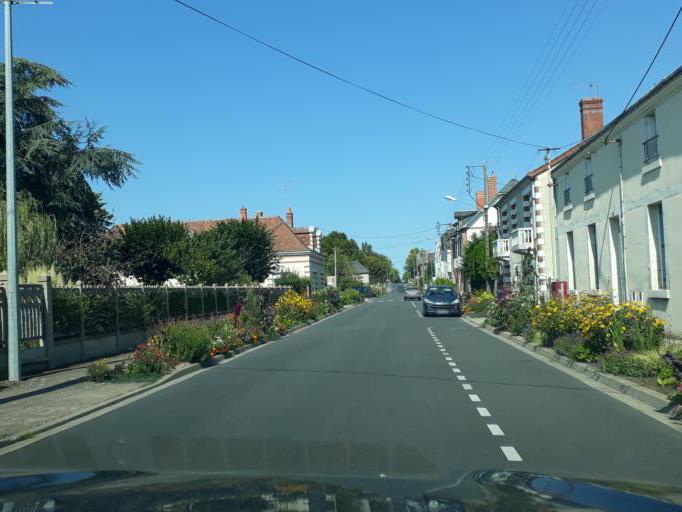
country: FR
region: Centre
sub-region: Departement de l'Indre
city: Chabris
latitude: 47.2577
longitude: 1.6554
